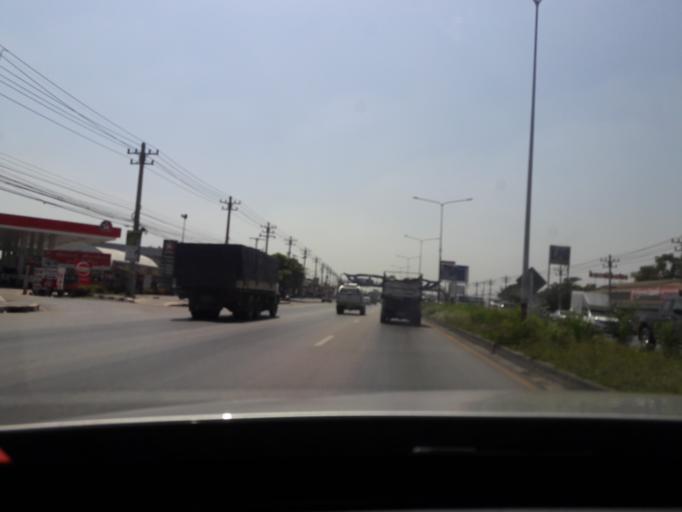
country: TH
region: Bangkok
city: Nong Khaem
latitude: 13.6821
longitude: 100.3220
